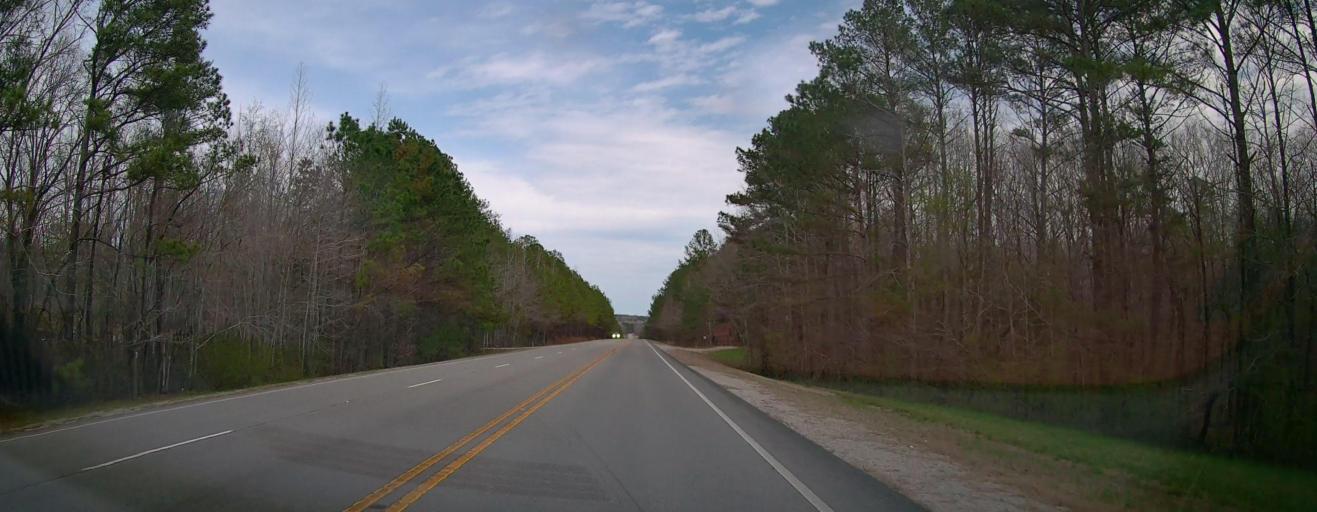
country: US
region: Alabama
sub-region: Marion County
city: Winfield
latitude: 33.9310
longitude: -87.7482
